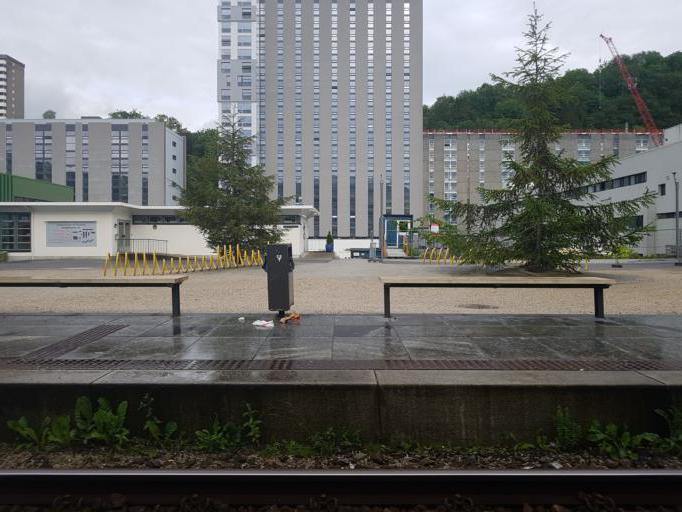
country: NO
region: Hordaland
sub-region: Bergen
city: Bergen
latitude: 60.3460
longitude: 5.3529
